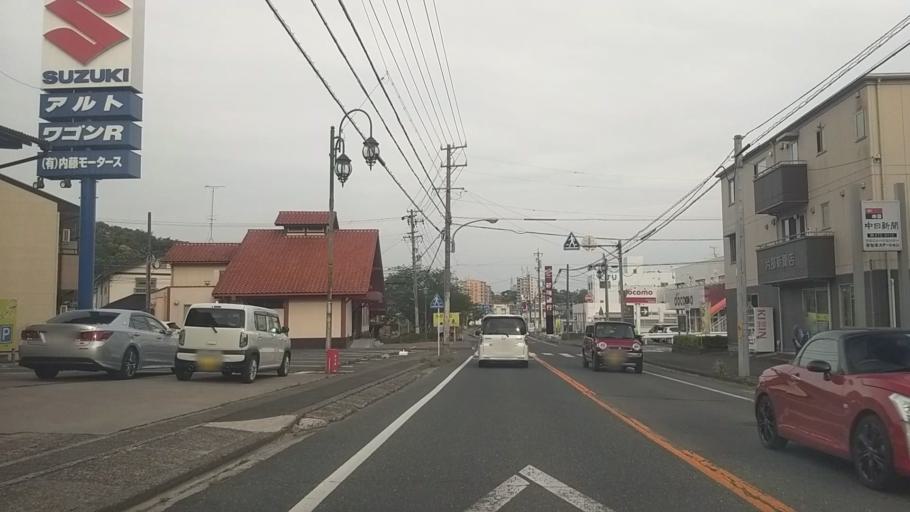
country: JP
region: Shizuoka
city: Hamamatsu
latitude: 34.7255
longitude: 137.6944
